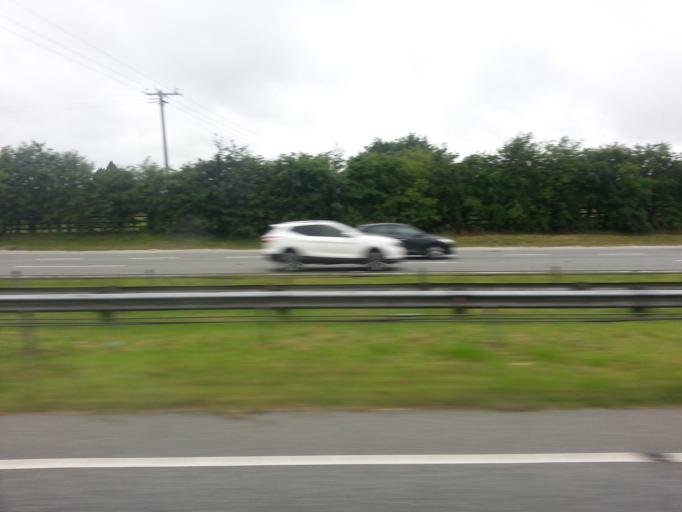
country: IE
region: Leinster
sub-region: Kildare
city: Johnstown
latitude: 53.2372
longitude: -6.6411
